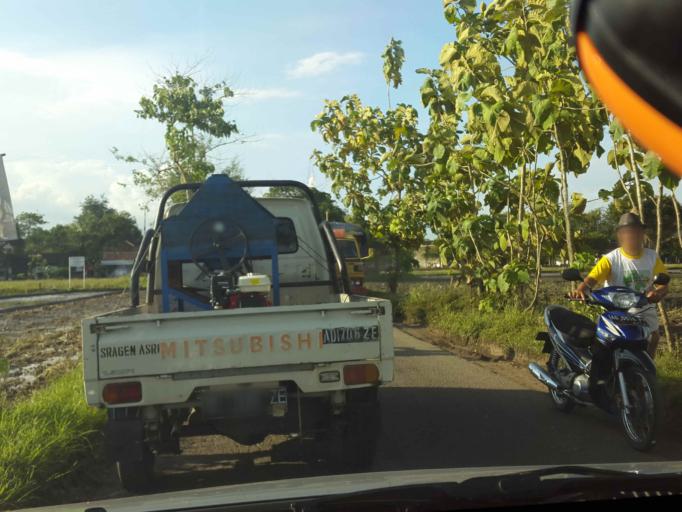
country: ID
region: Central Java
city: Sragen
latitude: -7.4203
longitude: 111.0627
